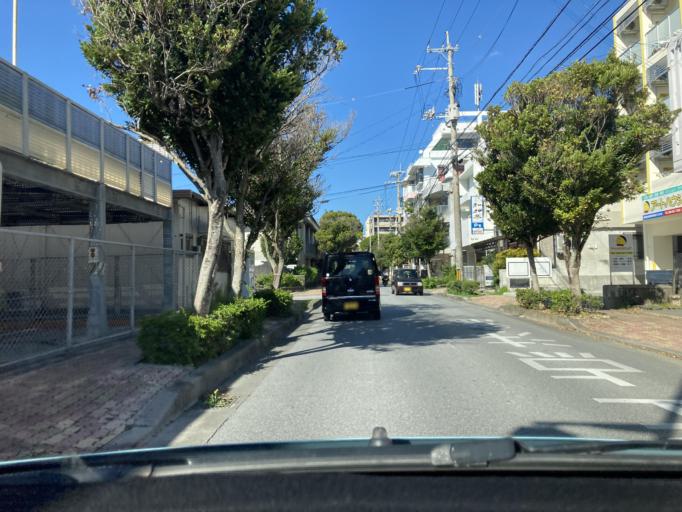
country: JP
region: Okinawa
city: Tomigusuku
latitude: 26.1887
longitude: 127.6592
